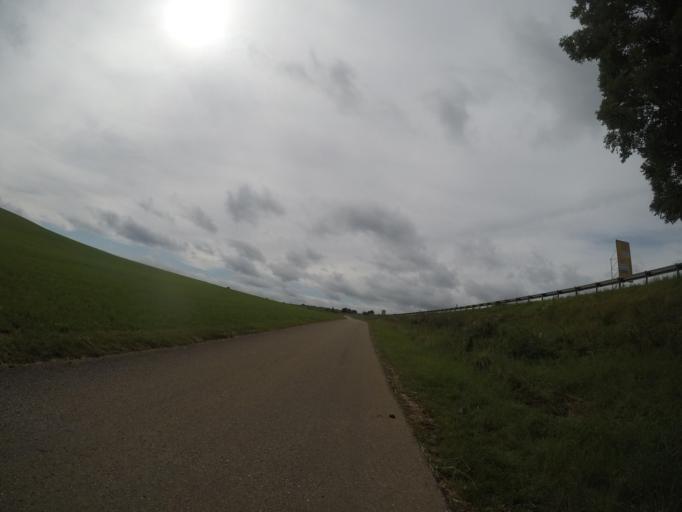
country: DE
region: Baden-Wuerttemberg
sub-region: Tuebingen Region
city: Laichingen
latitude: 48.4548
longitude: 9.6633
